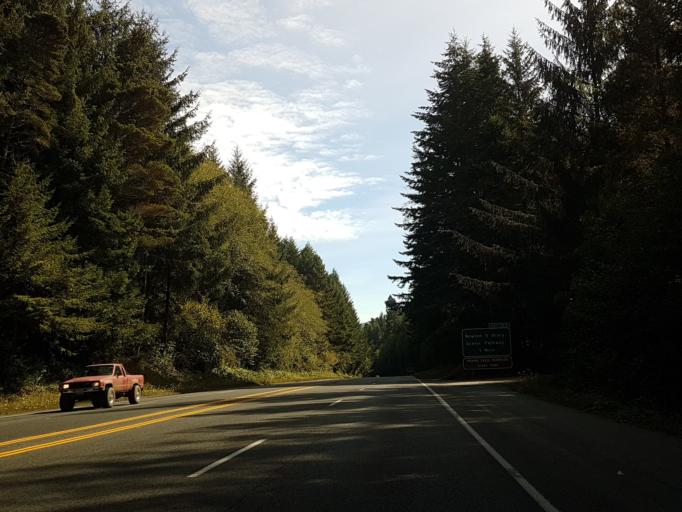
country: US
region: California
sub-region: Del Norte County
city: Bertsch-Oceanview
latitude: 41.4804
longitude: -124.0489
